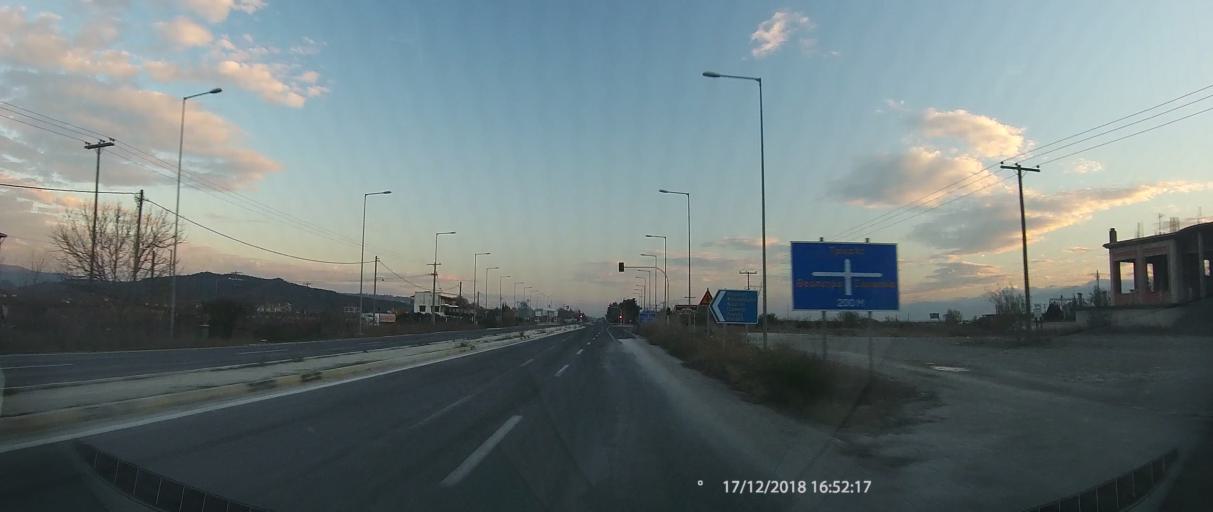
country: GR
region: Thessaly
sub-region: Trikala
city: Kalampaka
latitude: 39.6737
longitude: 21.6617
